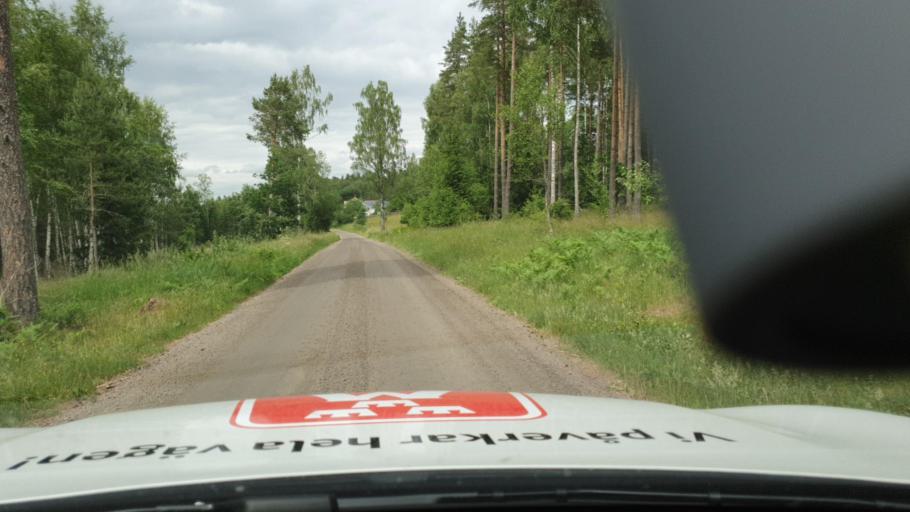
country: SE
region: Vaestra Goetaland
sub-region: Tidaholms Kommun
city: Olofstorp
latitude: 58.1827
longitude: 14.0492
